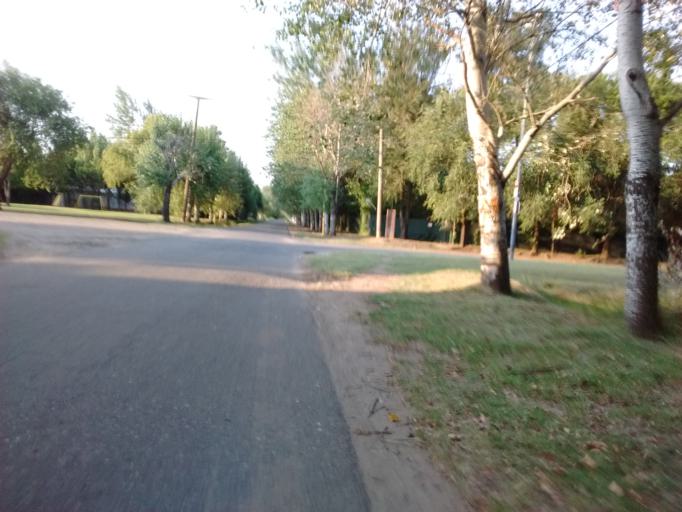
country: AR
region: Santa Fe
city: Funes
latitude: -32.9148
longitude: -60.7599
